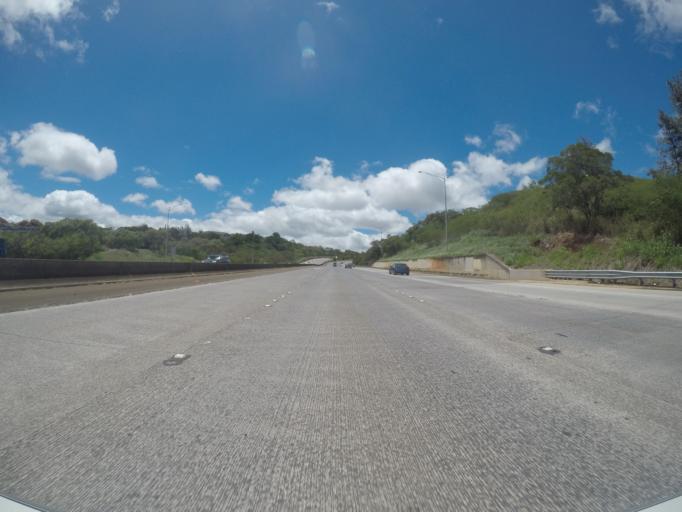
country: US
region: Hawaii
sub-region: Honolulu County
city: Waipio
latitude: 21.4137
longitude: -157.9909
